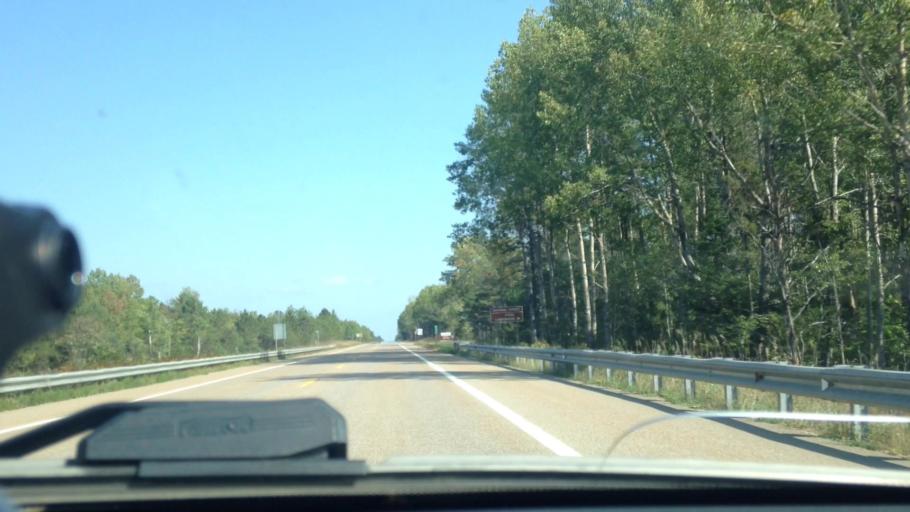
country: US
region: Michigan
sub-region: Mackinac County
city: Saint Ignace
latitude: 46.3584
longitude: -84.8658
